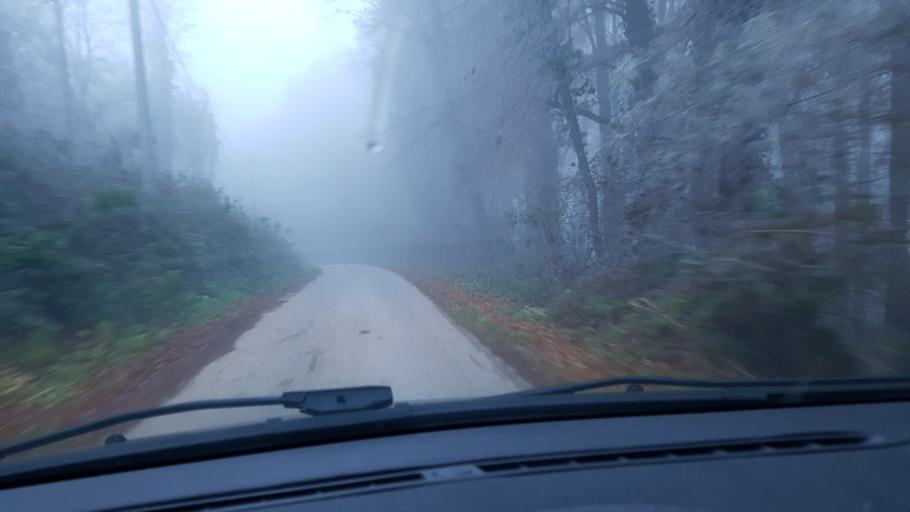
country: HR
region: Krapinsko-Zagorska
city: Pregrada
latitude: 46.2001
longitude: 15.7657
